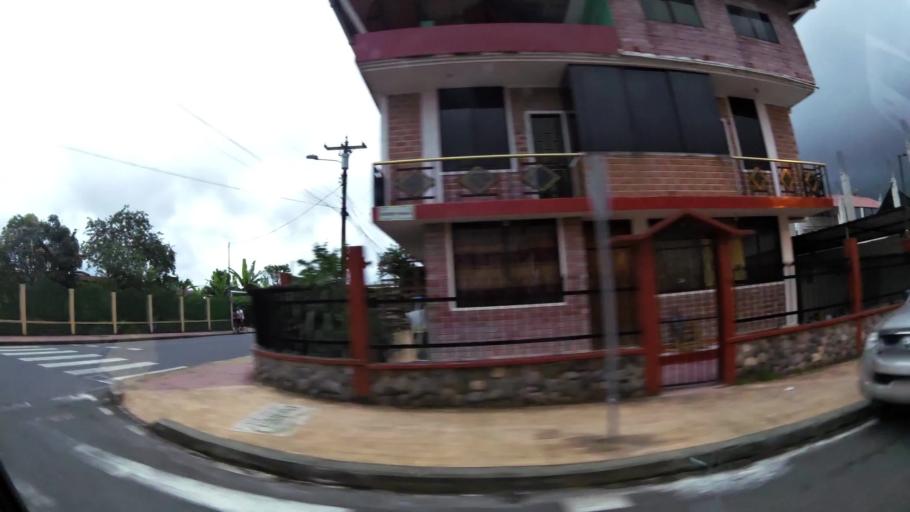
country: EC
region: Pastaza
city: Puyo
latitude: -1.4807
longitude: -78.0082
